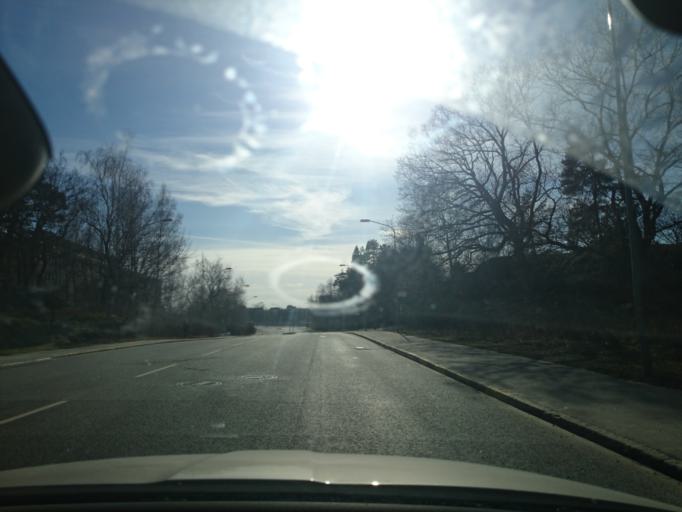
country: SE
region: Stockholm
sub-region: Haninge Kommun
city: Handen
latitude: 59.2386
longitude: 18.1116
